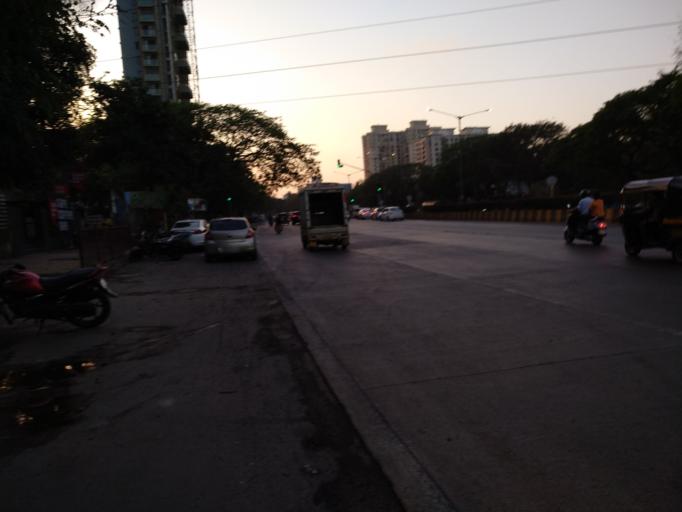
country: IN
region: Maharashtra
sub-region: Mumbai Suburban
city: Mumbai
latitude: 19.0442
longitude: 72.9189
